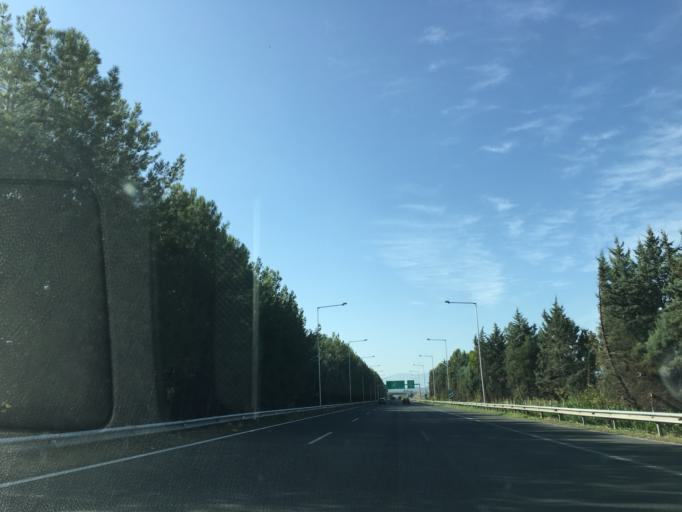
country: GR
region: Central Macedonia
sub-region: Nomos Pierias
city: Aiginio
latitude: 40.5169
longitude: 22.5715
